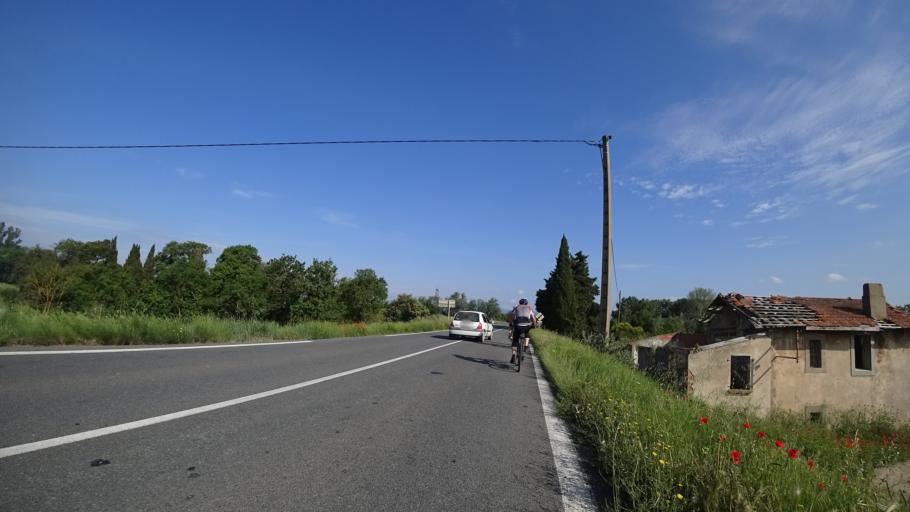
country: FR
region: Languedoc-Roussillon
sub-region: Departement de l'Herault
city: Olonzac
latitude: 43.2624
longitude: 2.7372
